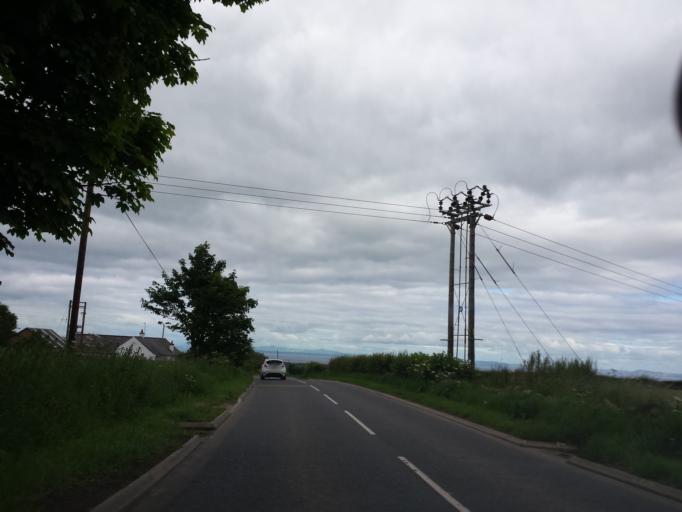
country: GB
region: Scotland
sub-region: East Lothian
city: Haddington
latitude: 55.9769
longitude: -2.8082
